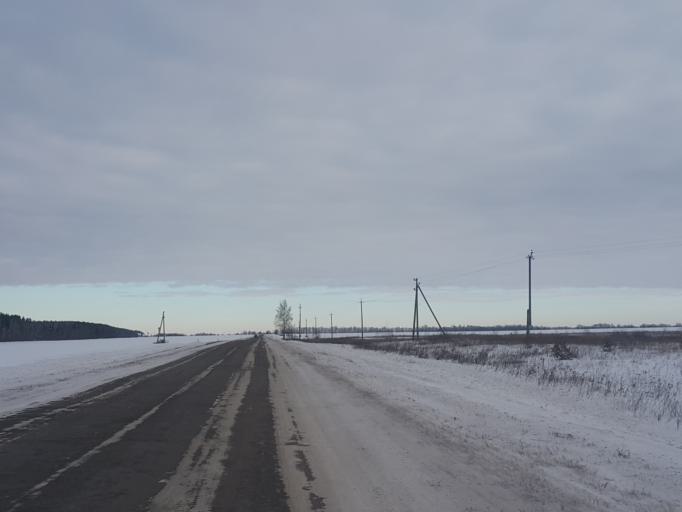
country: RU
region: Tambov
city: Novaya Lyada
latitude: 52.7537
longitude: 41.7193
